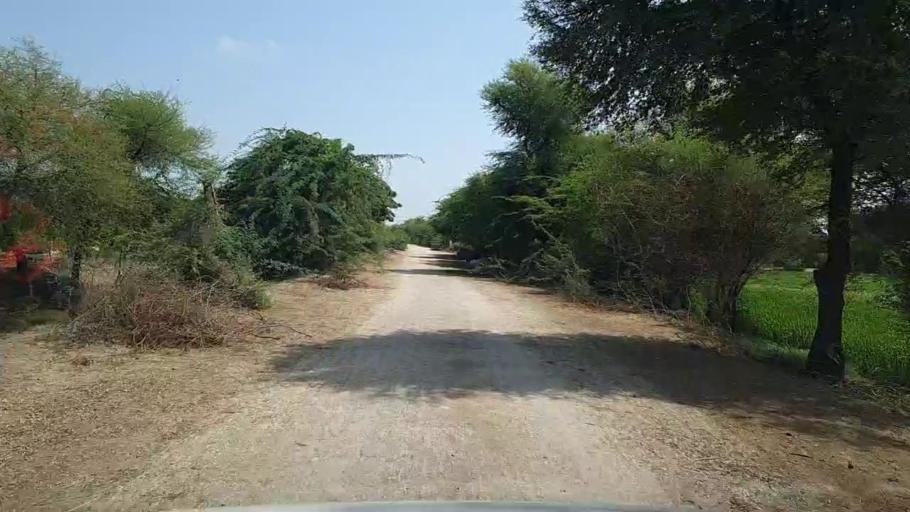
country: PK
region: Sindh
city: Kario
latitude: 24.8520
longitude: 68.6884
